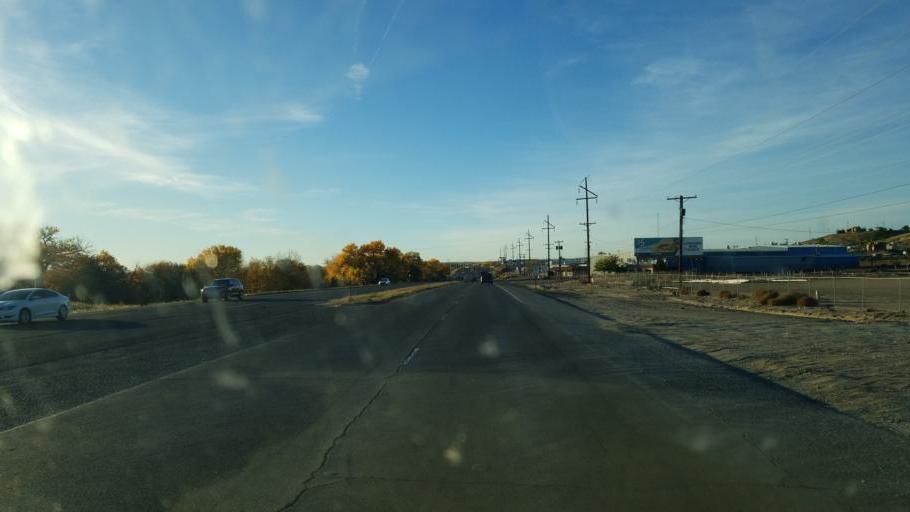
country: US
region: New Mexico
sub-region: San Juan County
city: Farmington
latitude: 36.7133
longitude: -108.1452
